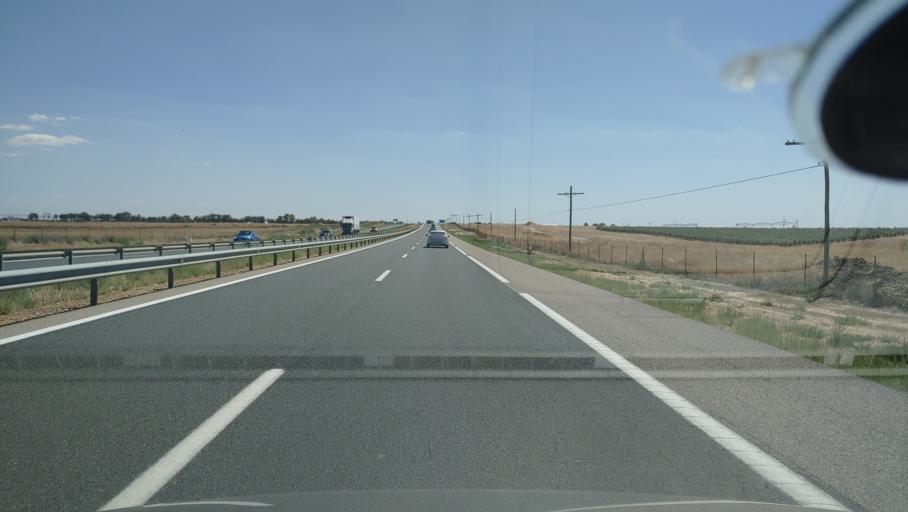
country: ES
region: Castille-La Mancha
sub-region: Provincia de Ciudad Real
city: Villarta de San Juan
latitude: 39.1397
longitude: -3.3828
